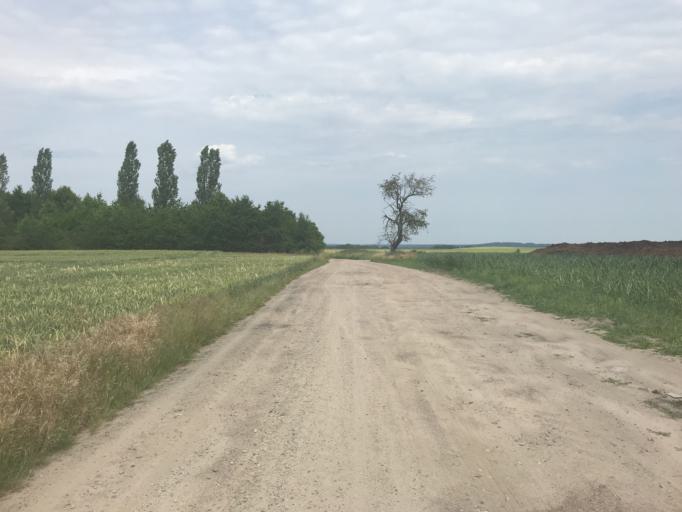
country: PL
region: West Pomeranian Voivodeship
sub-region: Powiat gryfinski
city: Chojna
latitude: 52.9211
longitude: 14.4360
